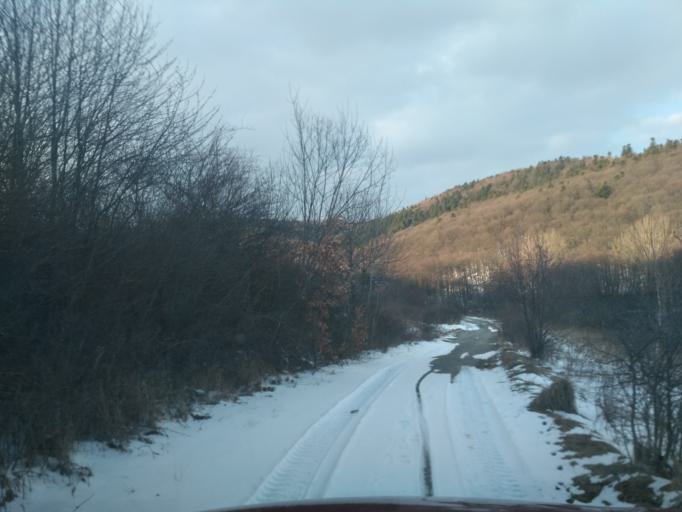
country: SK
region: Kosicky
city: Kosice
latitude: 48.7430
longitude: 21.1503
